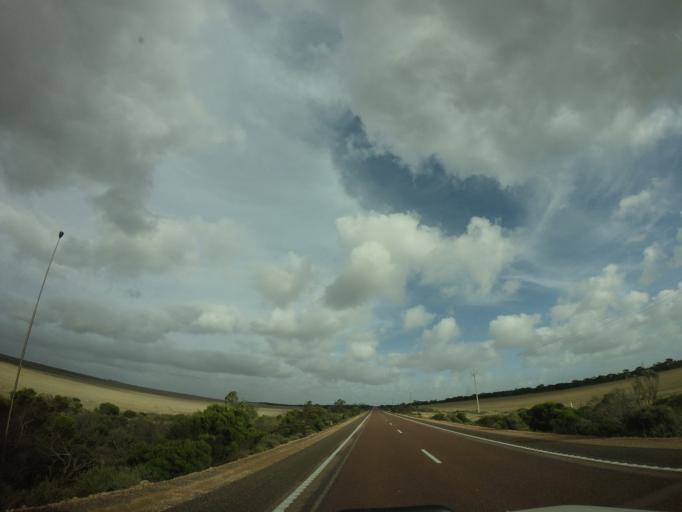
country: AU
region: South Australia
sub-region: Ceduna
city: Ceduna
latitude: -32.0615
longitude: 133.6188
